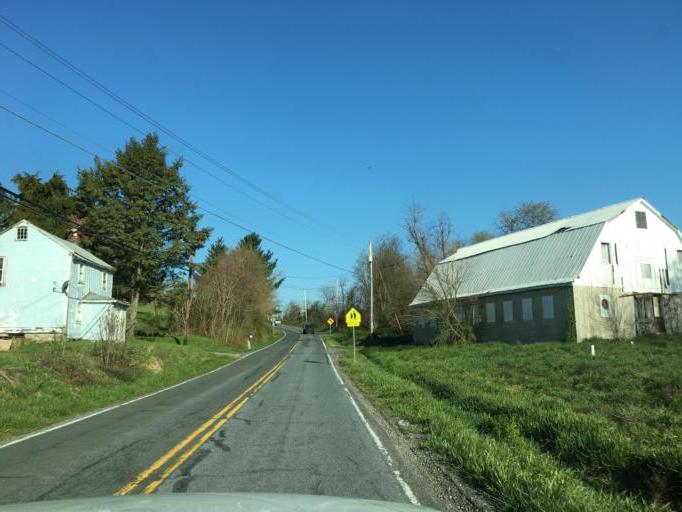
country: US
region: Maryland
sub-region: Frederick County
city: Linganore
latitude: 39.4845
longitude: -77.2511
